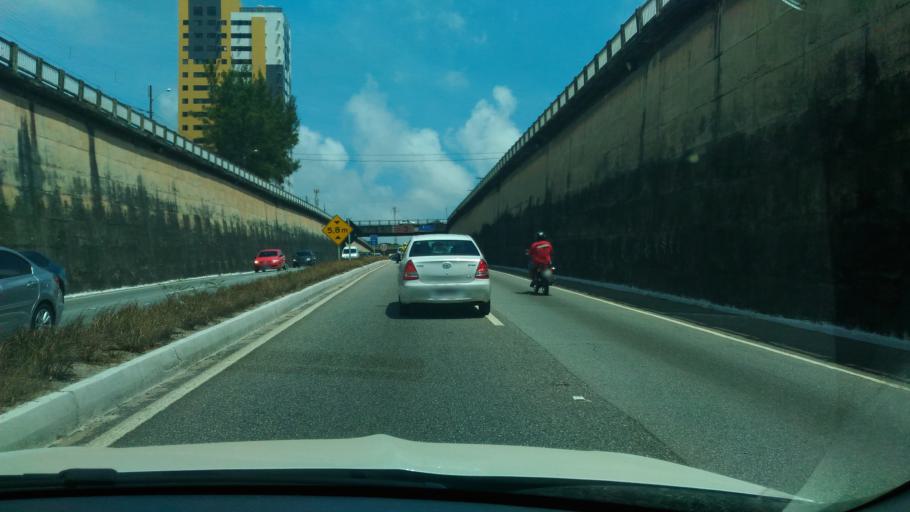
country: BR
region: Paraiba
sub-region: Joao Pessoa
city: Joao Pessoa
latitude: -7.1238
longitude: -34.8451
